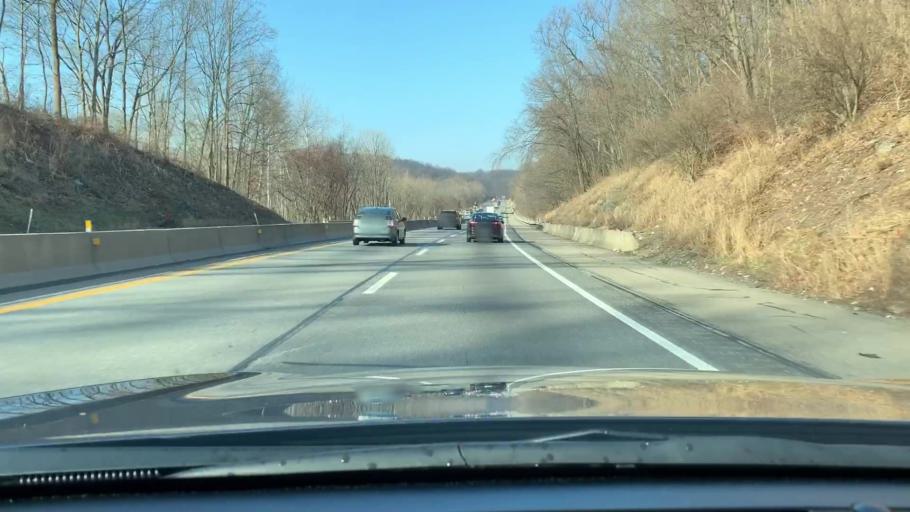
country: US
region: Pennsylvania
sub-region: Chester County
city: Downingtown
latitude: 40.0877
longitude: -75.7255
